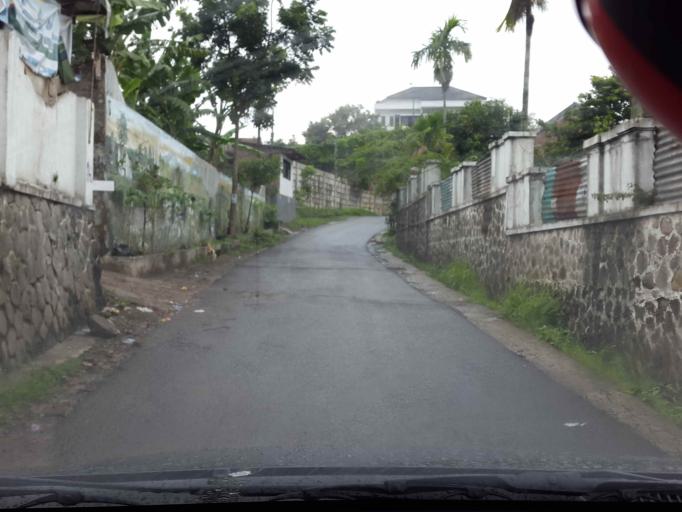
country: ID
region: West Java
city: Cimahi
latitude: -6.8801
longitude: 107.5655
